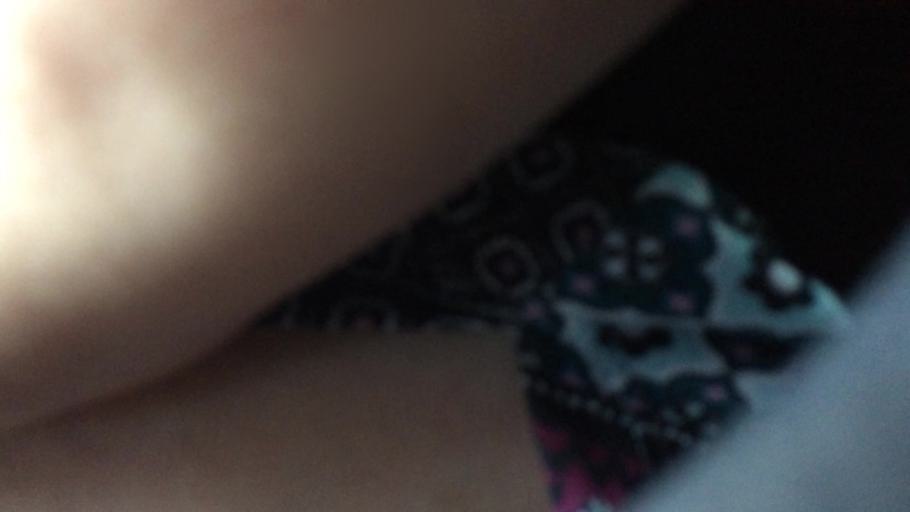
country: US
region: New Mexico
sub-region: Colfax County
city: Springer
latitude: 36.3455
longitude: -104.6097
